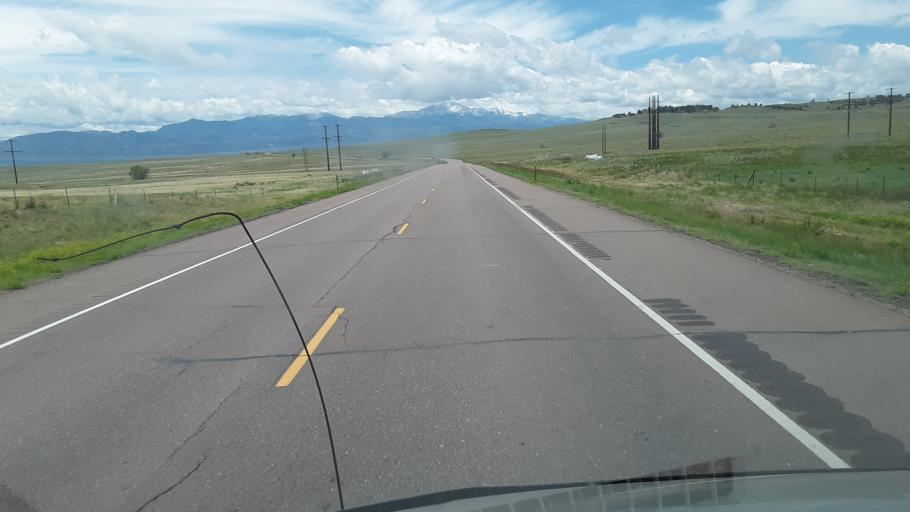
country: US
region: Colorado
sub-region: El Paso County
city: Cimarron Hills
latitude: 38.8389
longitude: -104.6210
